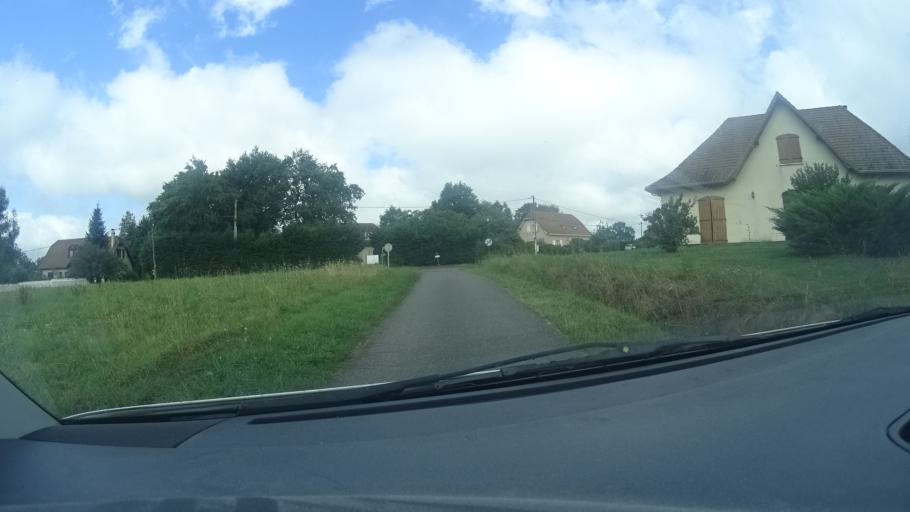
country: FR
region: Aquitaine
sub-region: Departement des Pyrenees-Atlantiques
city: Orthez
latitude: 43.4925
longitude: -0.7008
